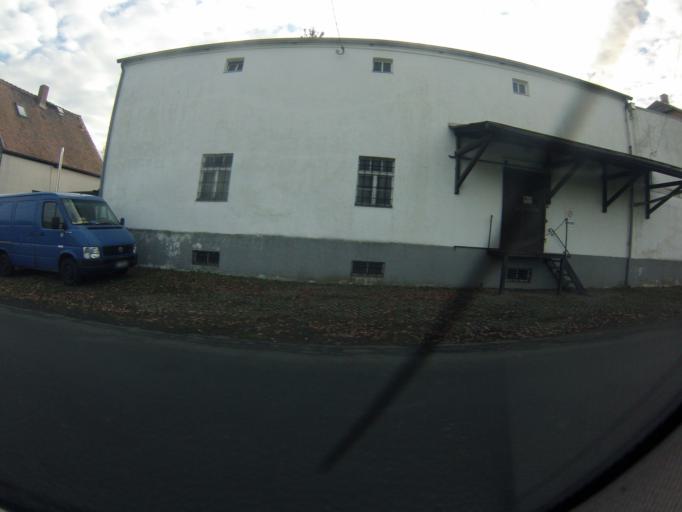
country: DE
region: Thuringia
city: Ponitz
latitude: 50.8579
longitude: 12.4142
